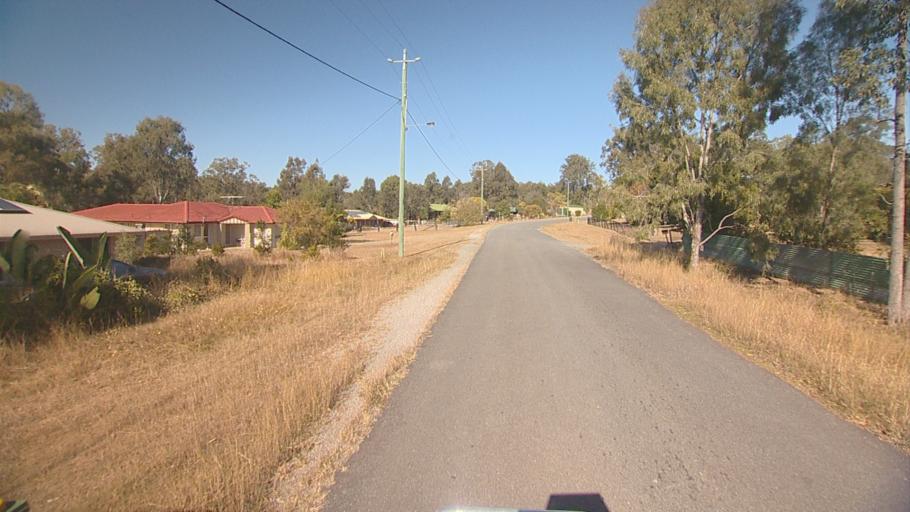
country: AU
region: Queensland
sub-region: Logan
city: Cedar Vale
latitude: -27.8694
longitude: 153.0068
